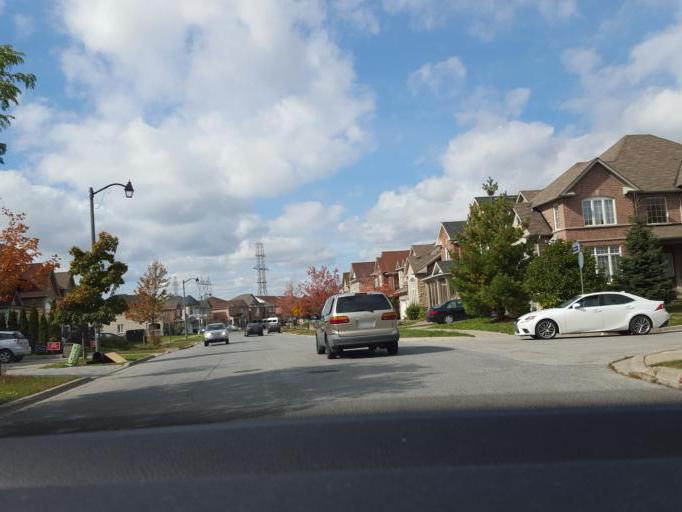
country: CA
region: Ontario
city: Markham
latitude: 43.8263
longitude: -79.2208
